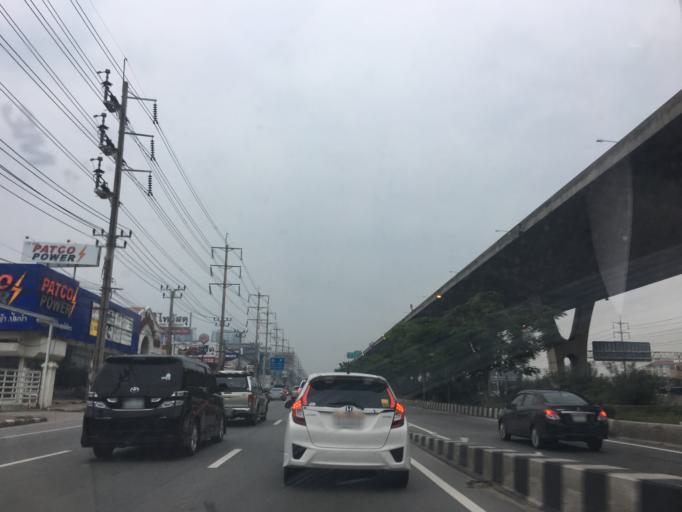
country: TH
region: Bangkok
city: Bang Na
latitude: 13.6512
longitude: 100.6787
